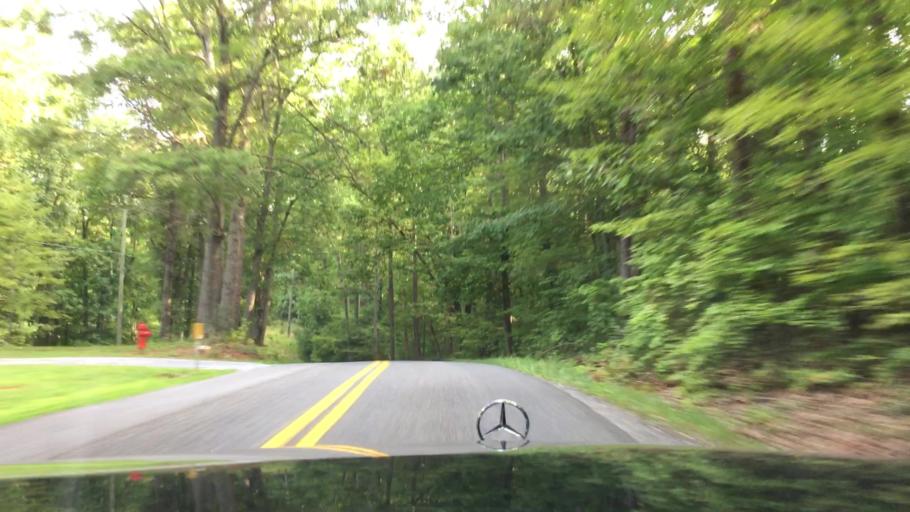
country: US
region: Virginia
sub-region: Campbell County
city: Timberlake
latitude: 37.2681
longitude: -79.2642
